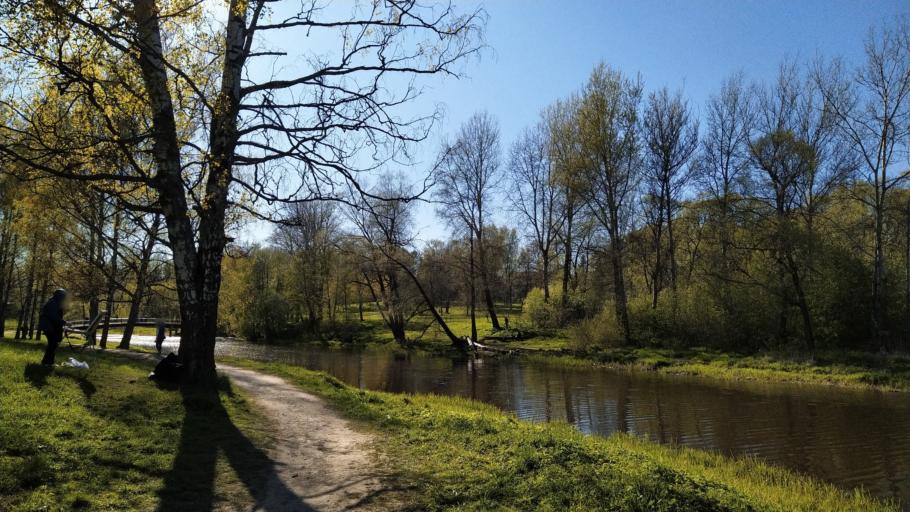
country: RU
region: St.-Petersburg
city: Pavlovsk
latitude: 59.6824
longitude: 30.4474
